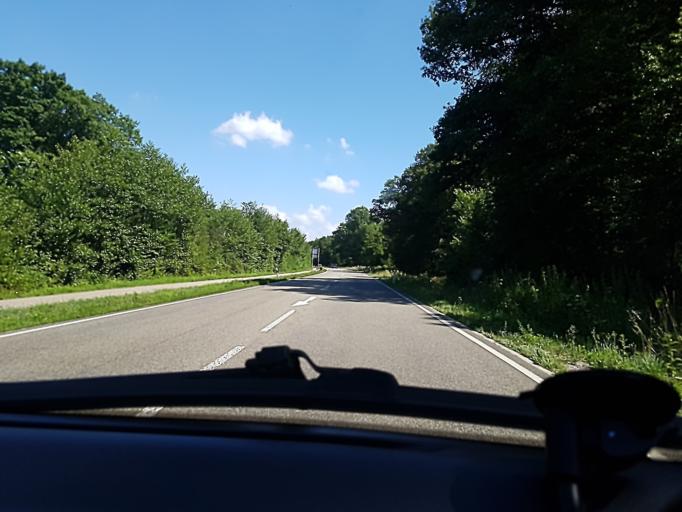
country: DE
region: Baden-Wuerttemberg
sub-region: Freiburg Region
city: Schutterwald
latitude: 48.4861
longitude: 7.8621
